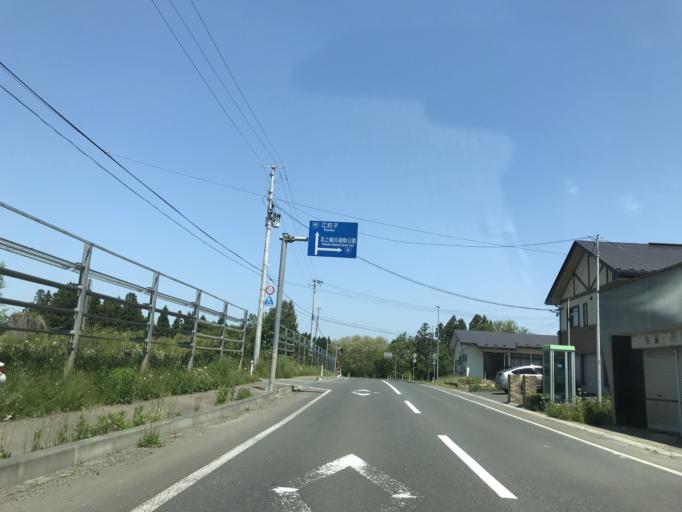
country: JP
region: Iwate
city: Kitakami
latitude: 39.2609
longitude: 141.0635
